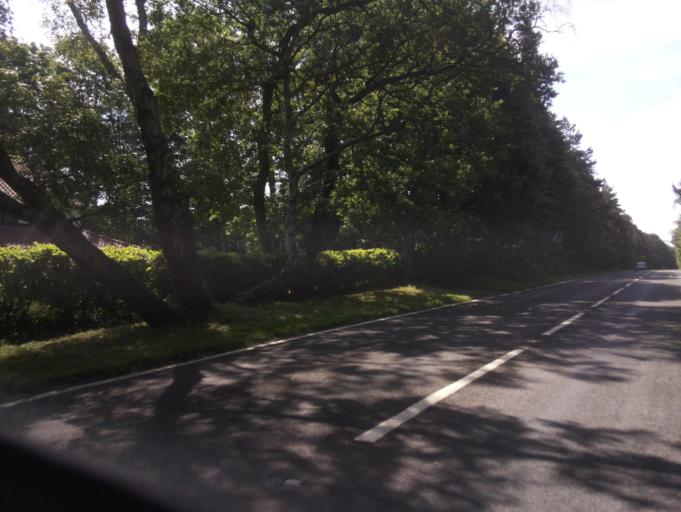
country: GB
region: England
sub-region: North Lincolnshire
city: Manton
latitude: 53.5301
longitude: -0.5775
